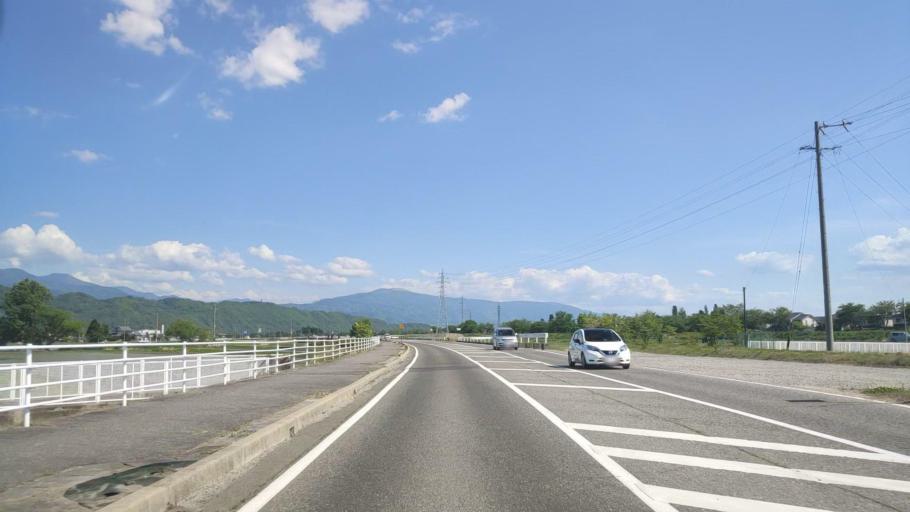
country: JP
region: Nagano
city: Toyoshina
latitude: 36.2839
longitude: 137.9113
